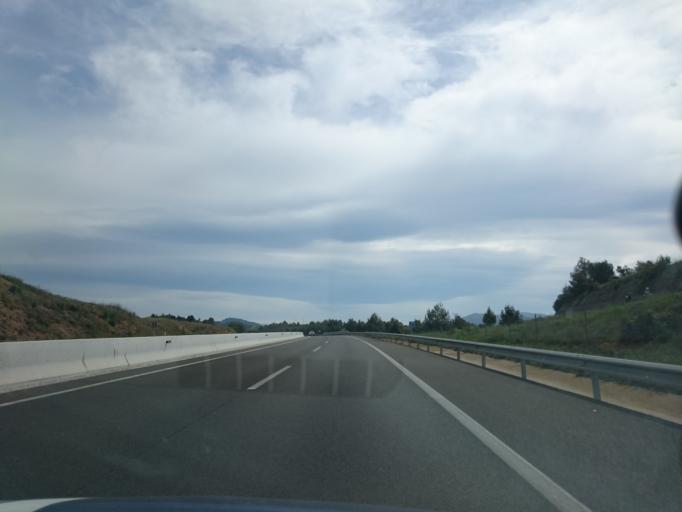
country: ES
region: Catalonia
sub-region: Provincia de Barcelona
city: Santa Maria d'Olo
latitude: 41.8844
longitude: 2.0407
